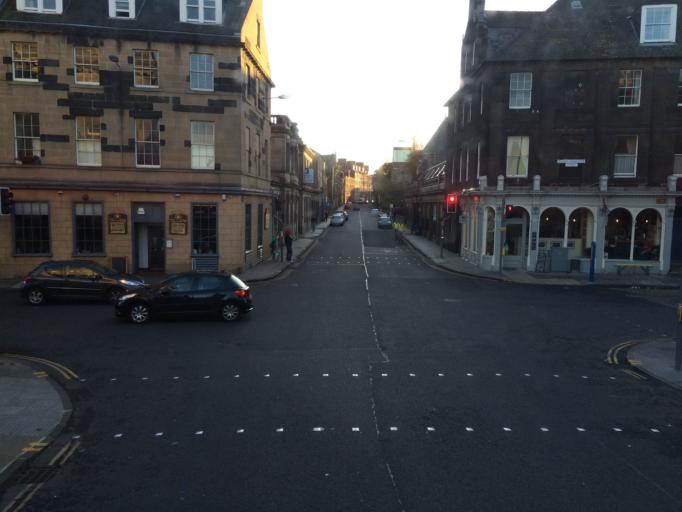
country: GB
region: Scotland
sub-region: West Lothian
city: Seafield
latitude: 55.9737
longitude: -3.1677
